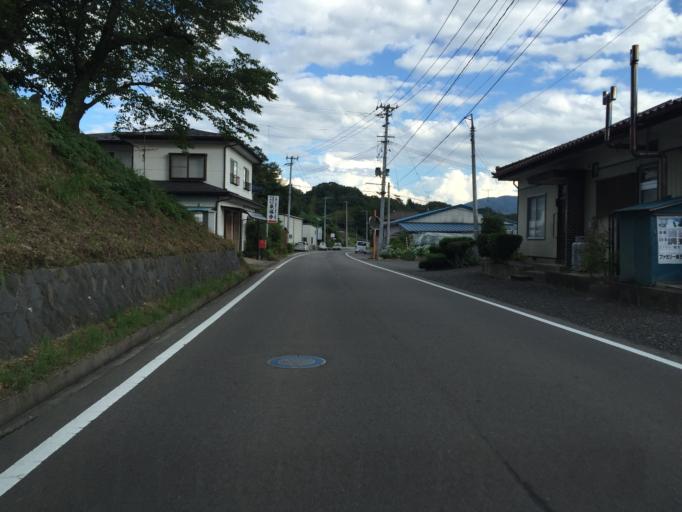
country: JP
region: Fukushima
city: Fukushima-shi
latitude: 37.6749
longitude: 140.5846
